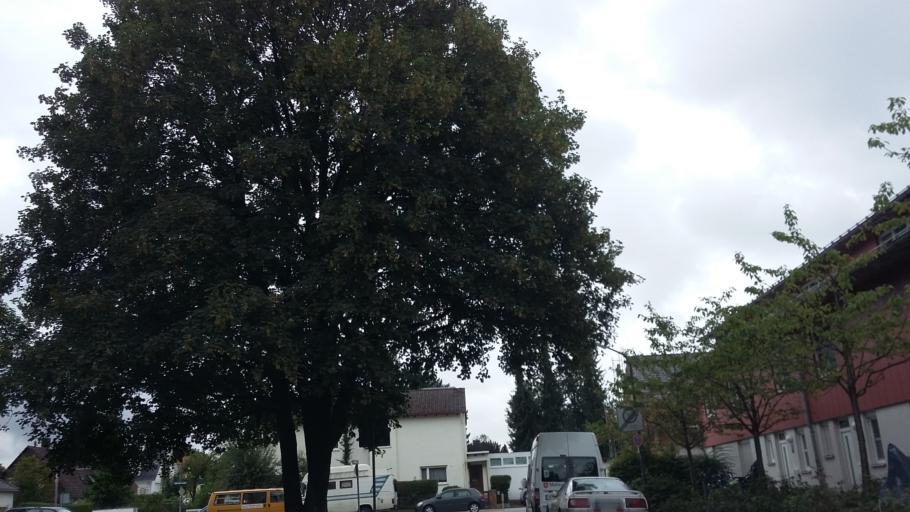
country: DE
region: Bavaria
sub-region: Upper Bavaria
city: Grafelfing
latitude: 48.1482
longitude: 11.4227
